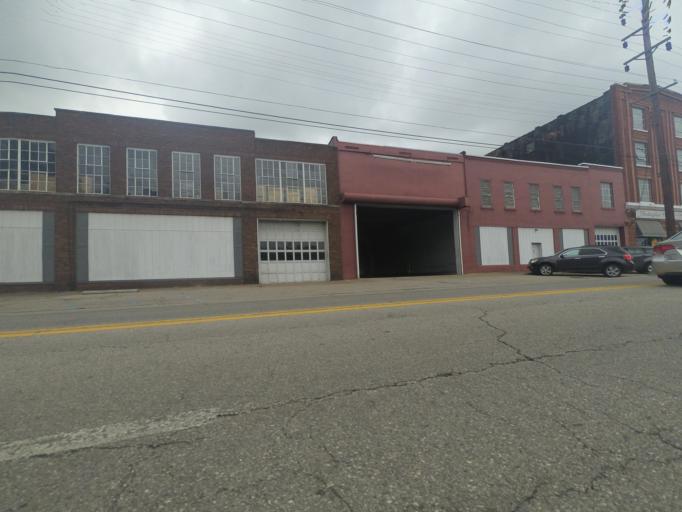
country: US
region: West Virginia
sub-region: Cabell County
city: Huntington
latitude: 38.4145
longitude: -82.4452
